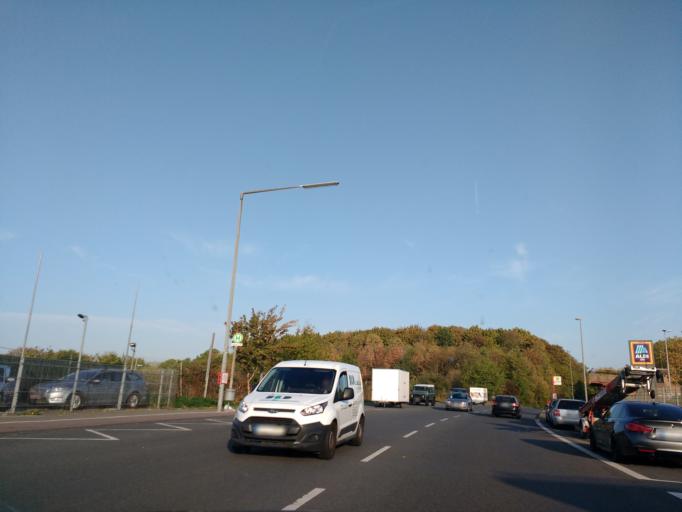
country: DE
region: North Rhine-Westphalia
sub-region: Regierungsbezirk Koln
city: Bilderstoeckchen
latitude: 50.9834
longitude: 6.9135
